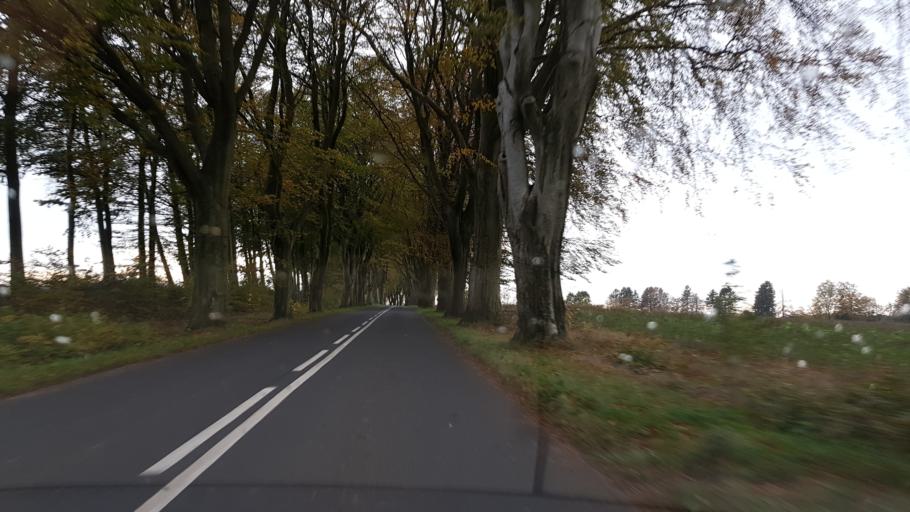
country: PL
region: West Pomeranian Voivodeship
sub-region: Powiat koszalinski
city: Polanow
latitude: 54.1413
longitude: 16.5445
